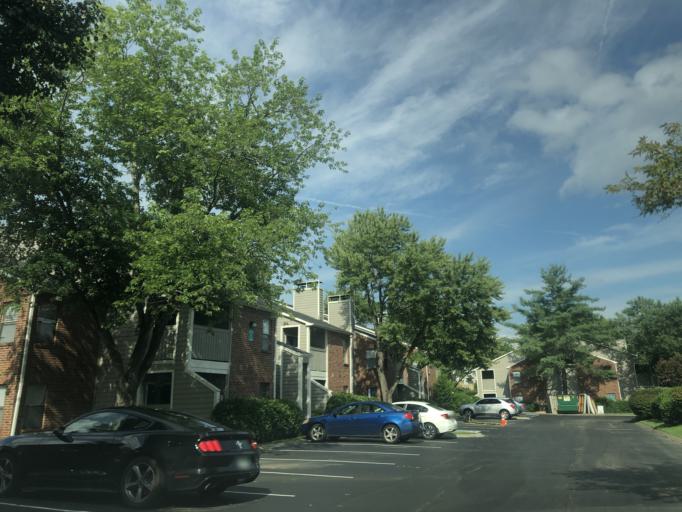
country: US
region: Tennessee
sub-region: Davidson County
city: Lakewood
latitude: 36.1607
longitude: -86.6472
